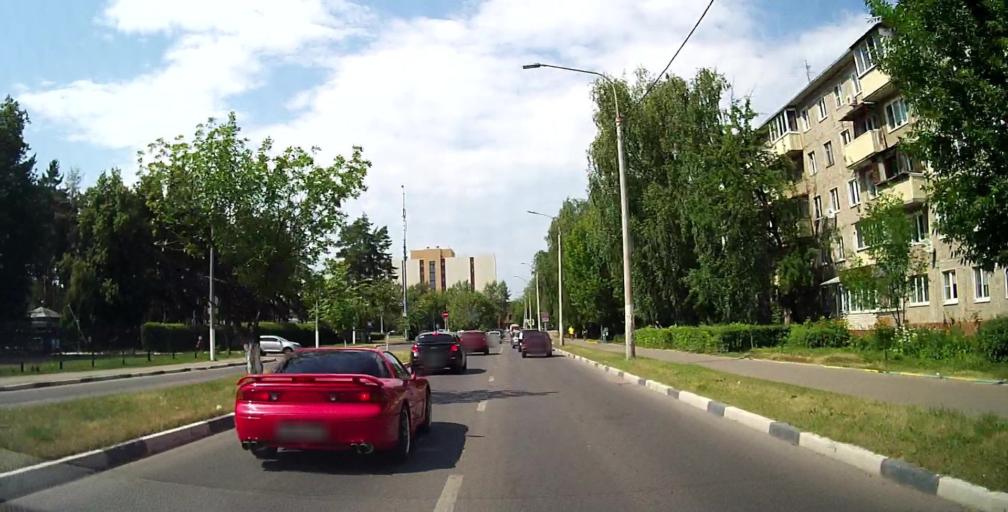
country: RU
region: Moskovskaya
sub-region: Podol'skiy Rayon
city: Podol'sk
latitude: 55.4201
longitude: 37.5185
